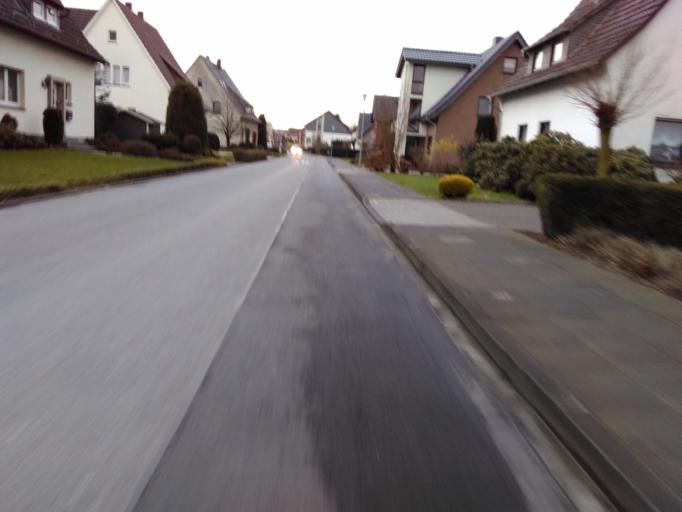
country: DE
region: North Rhine-Westphalia
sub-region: Regierungsbezirk Detmold
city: Verl
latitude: 51.8830
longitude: 8.4995
